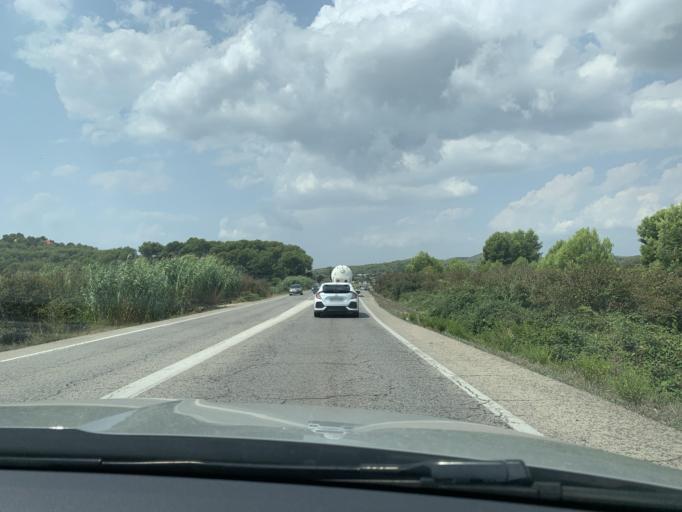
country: ES
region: Catalonia
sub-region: Provincia de Tarragona
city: Altafulla
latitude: 41.1402
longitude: 1.3600
